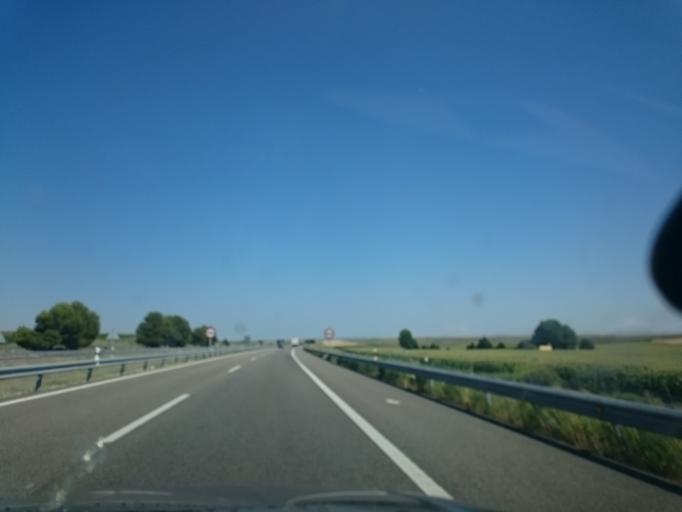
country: ES
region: Aragon
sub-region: Provincia de Zaragoza
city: Bujaraloz
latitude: 41.5222
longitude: -0.1603
